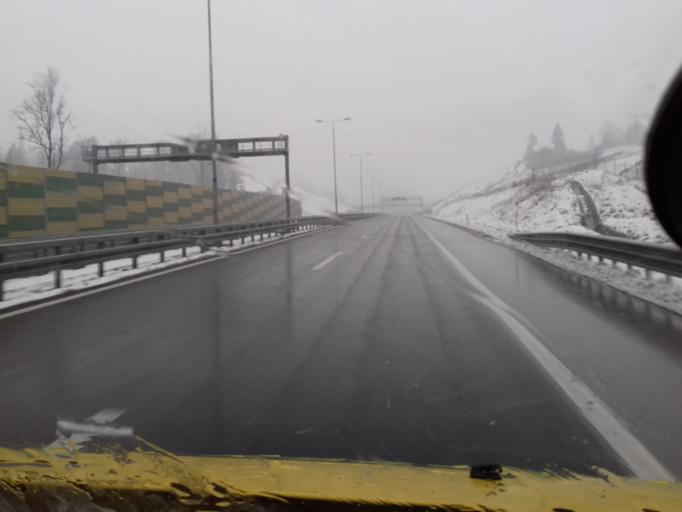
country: BA
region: Federation of Bosnia and Herzegovina
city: Hadzici
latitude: 43.8624
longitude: 18.2656
